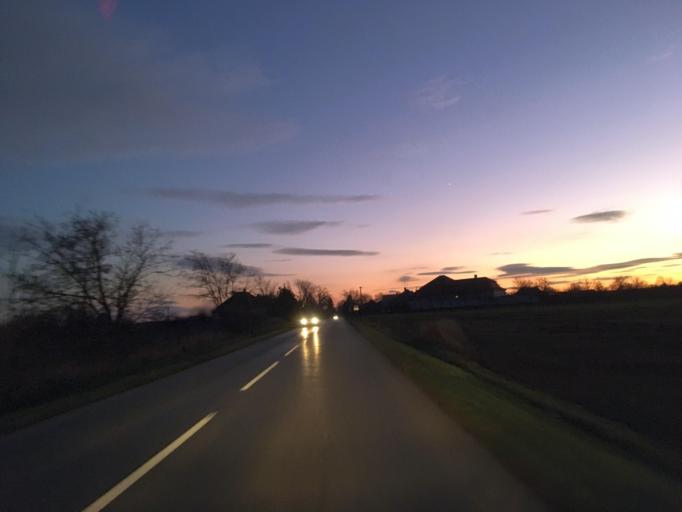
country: SK
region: Nitriansky
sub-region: Okres Komarno
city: Hurbanovo
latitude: 47.9136
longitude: 18.1366
